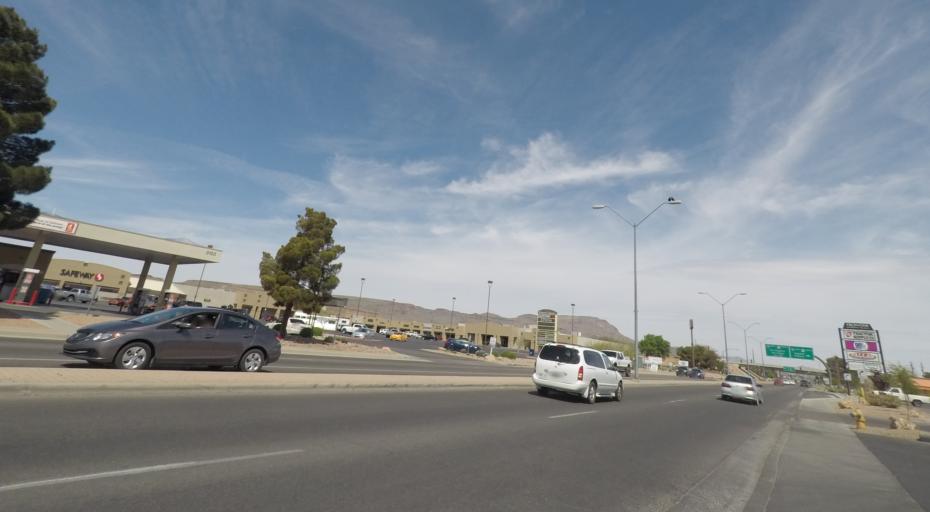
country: US
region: Arizona
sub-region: Mohave County
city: Kingman
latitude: 35.2143
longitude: -114.0351
